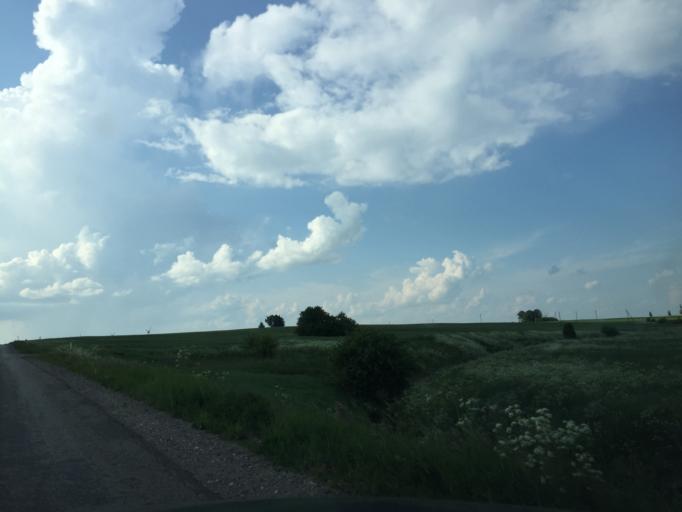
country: LT
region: Klaipedos apskritis
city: Kretinga
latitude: 55.9298
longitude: 21.1977
